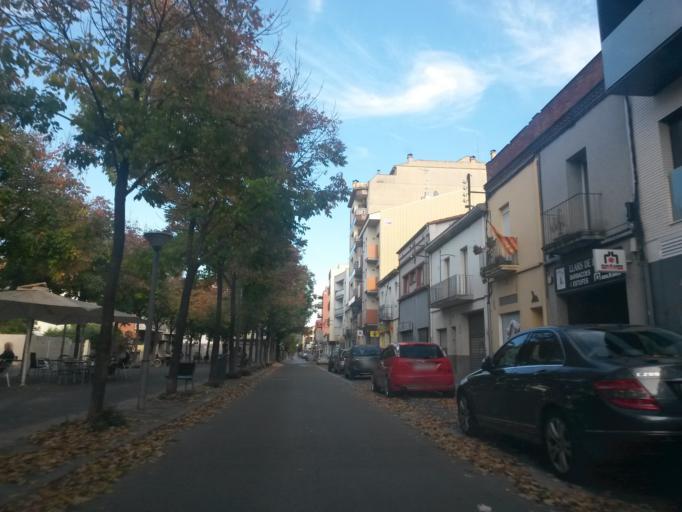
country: ES
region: Catalonia
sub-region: Provincia de Girona
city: Salt
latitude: 41.9756
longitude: 2.7946
